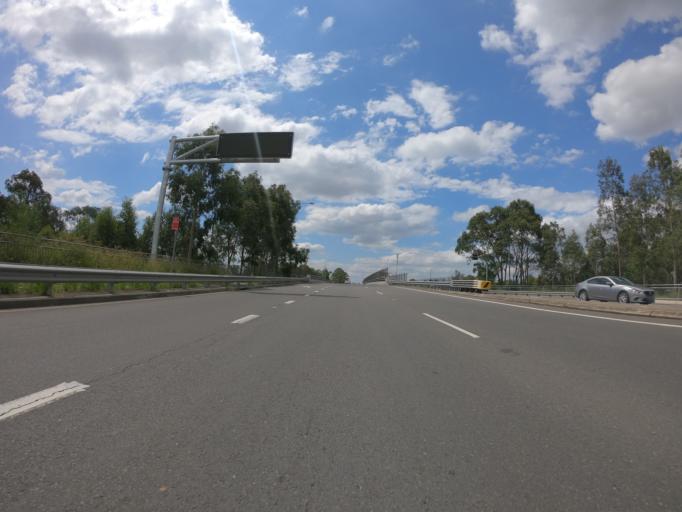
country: AU
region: New South Wales
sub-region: Blacktown
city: Mount Druitt
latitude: -33.7849
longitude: 150.7707
